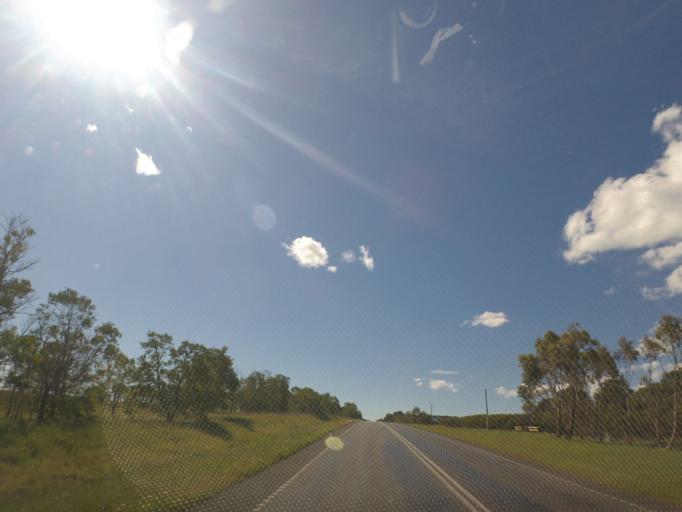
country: AU
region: Victoria
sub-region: Moorabool
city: Bacchus Marsh
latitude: -37.6554
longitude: 144.2301
